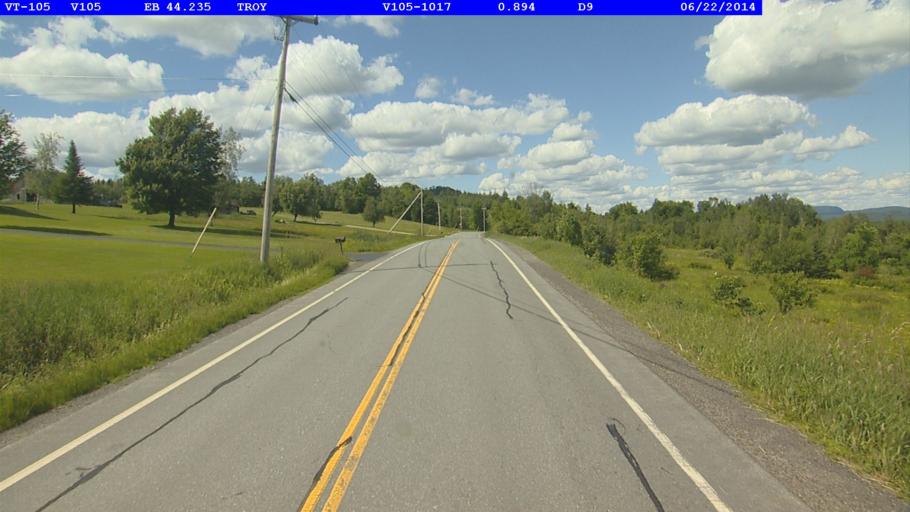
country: US
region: Vermont
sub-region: Orleans County
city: Newport
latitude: 44.9716
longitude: -72.4140
